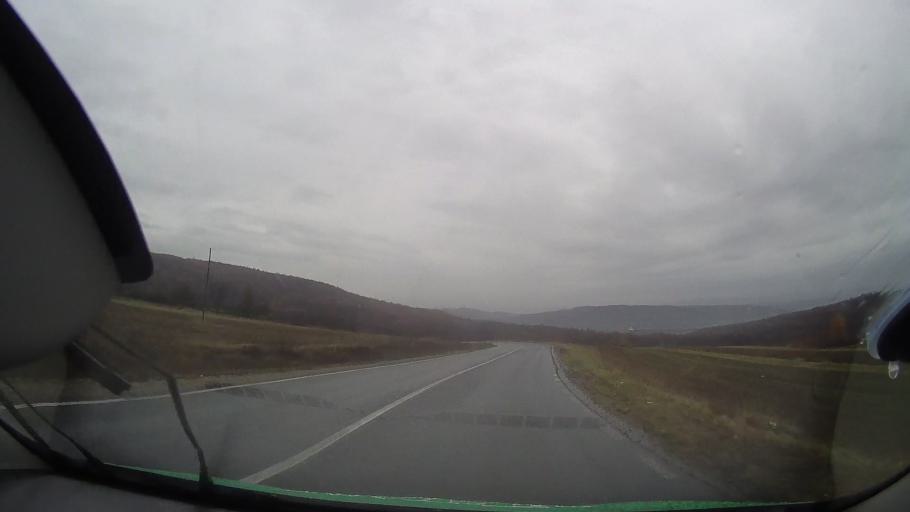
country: RO
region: Bihor
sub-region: Comuna Rabagani
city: Rabagani
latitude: 46.7289
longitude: 22.2343
